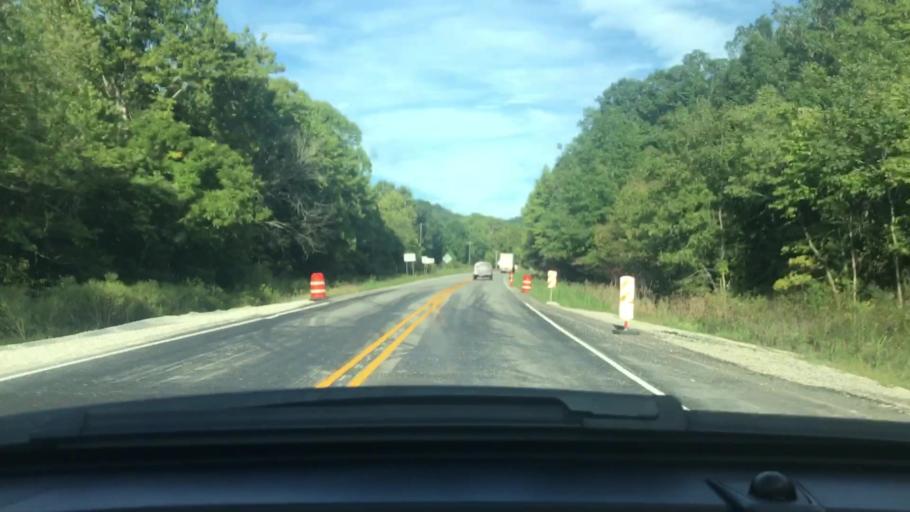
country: US
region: Arkansas
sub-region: Sharp County
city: Cherokee Village
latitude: 36.3032
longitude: -91.4258
